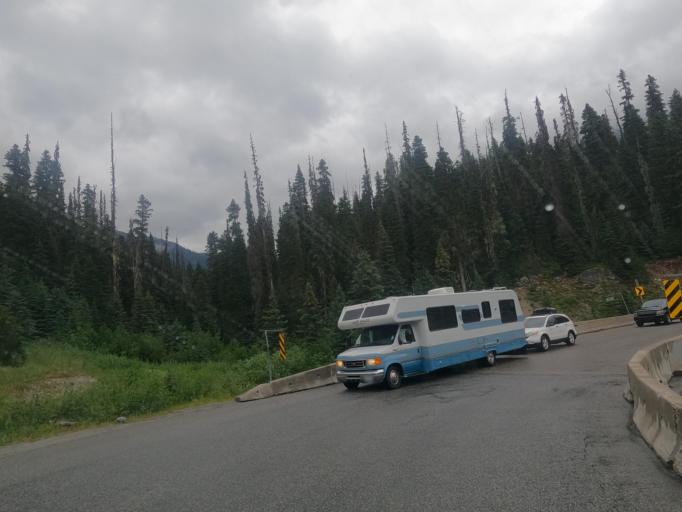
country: CA
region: British Columbia
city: Pemberton
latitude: 50.3847
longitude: -122.4697
